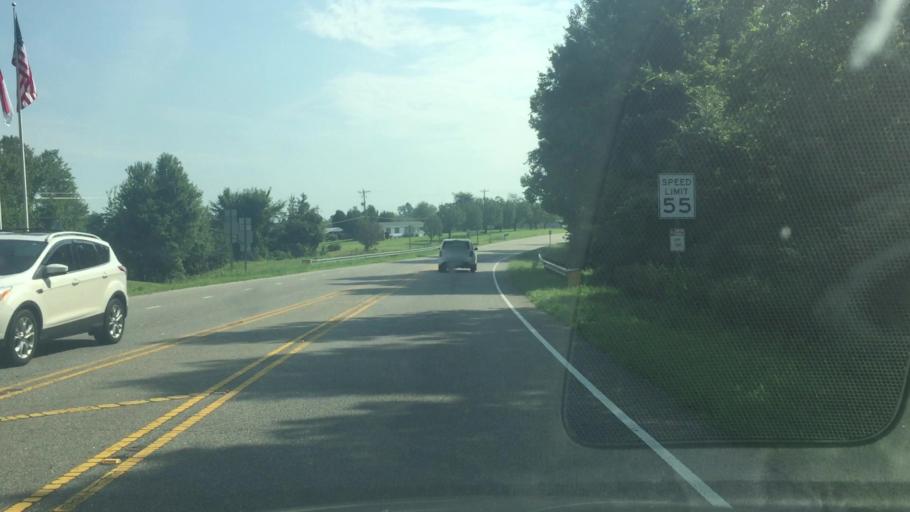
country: US
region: North Carolina
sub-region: Columbus County
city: Tabor City
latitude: 34.1570
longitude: -78.8573
